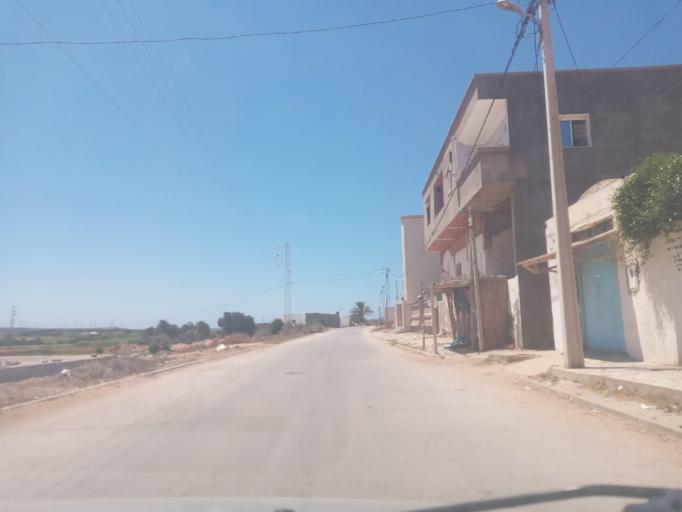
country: TN
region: Nabul
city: El Haouaria
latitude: 37.0506
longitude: 11.0011
